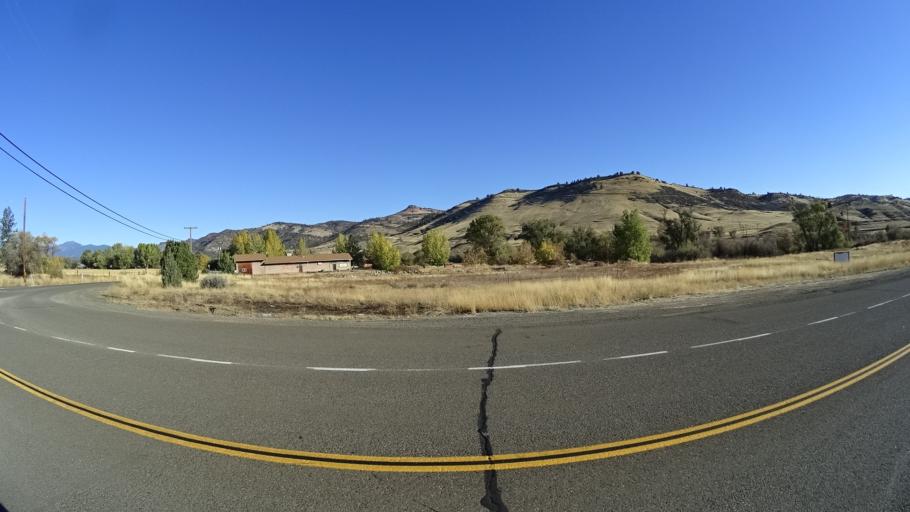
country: US
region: California
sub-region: Siskiyou County
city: Montague
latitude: 41.8981
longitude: -122.5511
